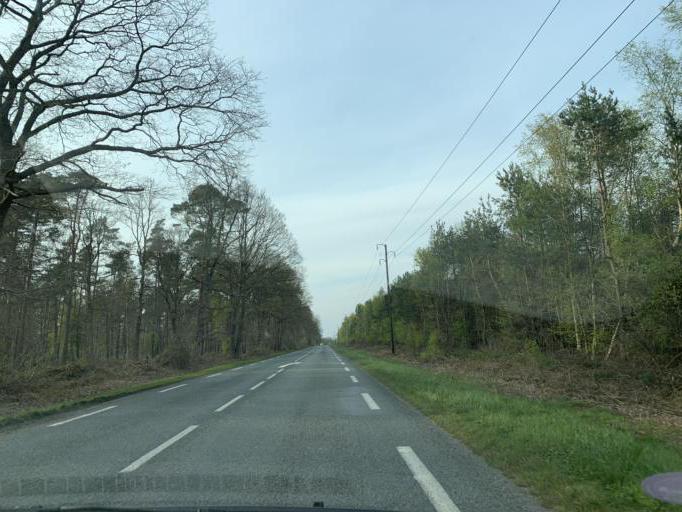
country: FR
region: Haute-Normandie
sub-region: Departement de la Seine-Maritime
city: Jumieges
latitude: 49.4224
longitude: 0.7935
